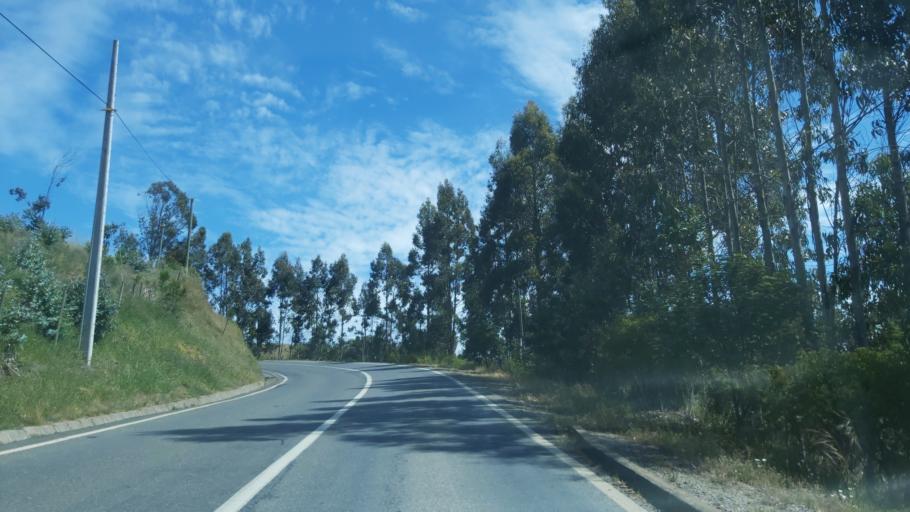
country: CL
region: Maule
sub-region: Provincia de Talca
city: Constitucion
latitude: -35.5696
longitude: -72.6034
